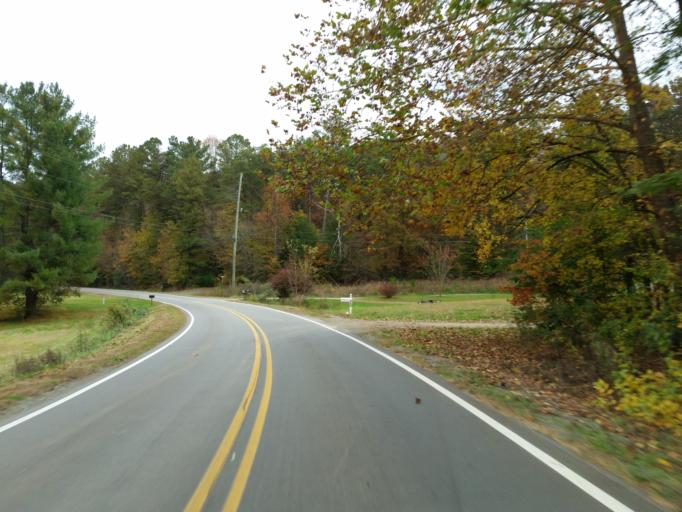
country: US
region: Georgia
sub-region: Gilmer County
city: Ellijay
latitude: 34.6554
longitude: -84.3804
